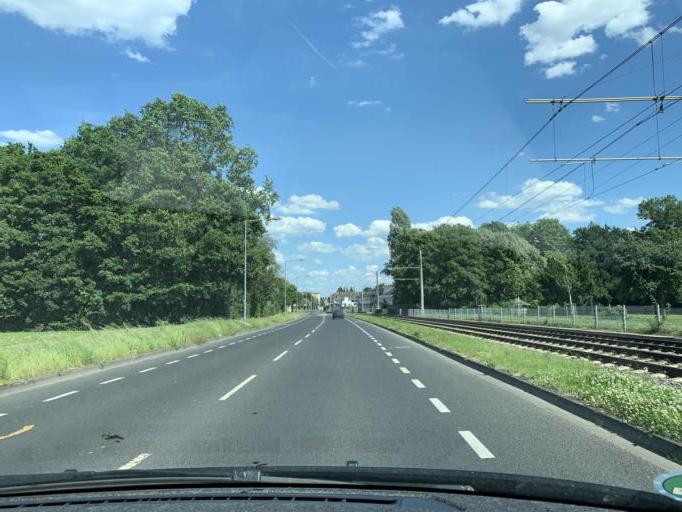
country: DE
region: North Rhine-Westphalia
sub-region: Regierungsbezirk Koln
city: Bilderstoeckchen
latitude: 50.9950
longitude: 6.9226
